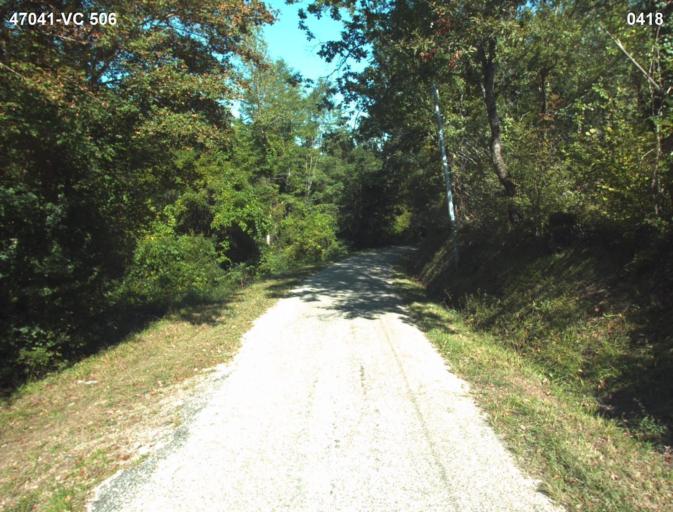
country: FR
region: Aquitaine
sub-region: Departement du Lot-et-Garonne
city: Port-Sainte-Marie
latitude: 44.2098
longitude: 0.3853
